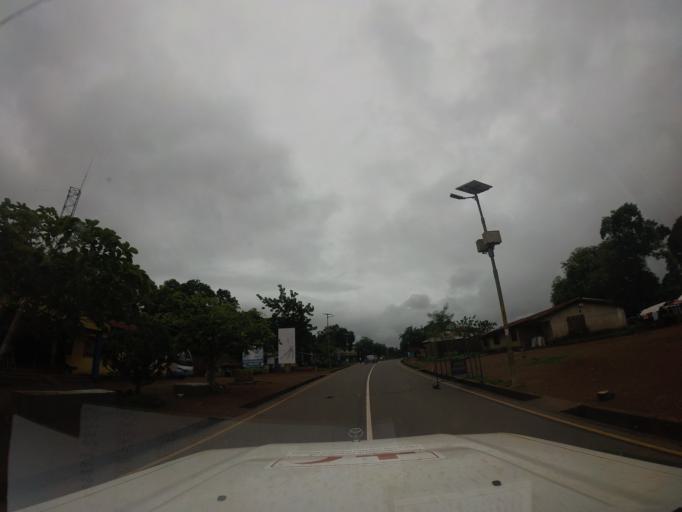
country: SL
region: Northern Province
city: Kambia
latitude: 9.1213
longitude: -12.9185
